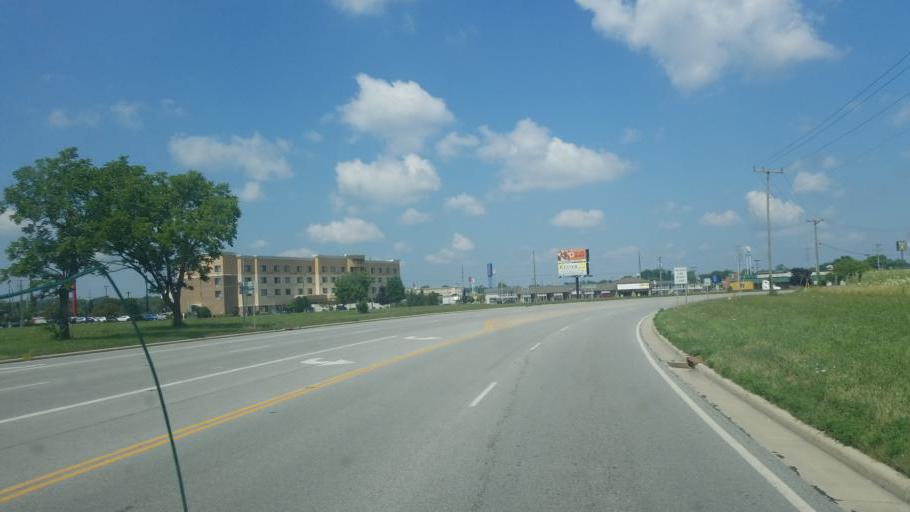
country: US
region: Ohio
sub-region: Allen County
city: Lima
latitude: 40.7279
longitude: -84.0691
